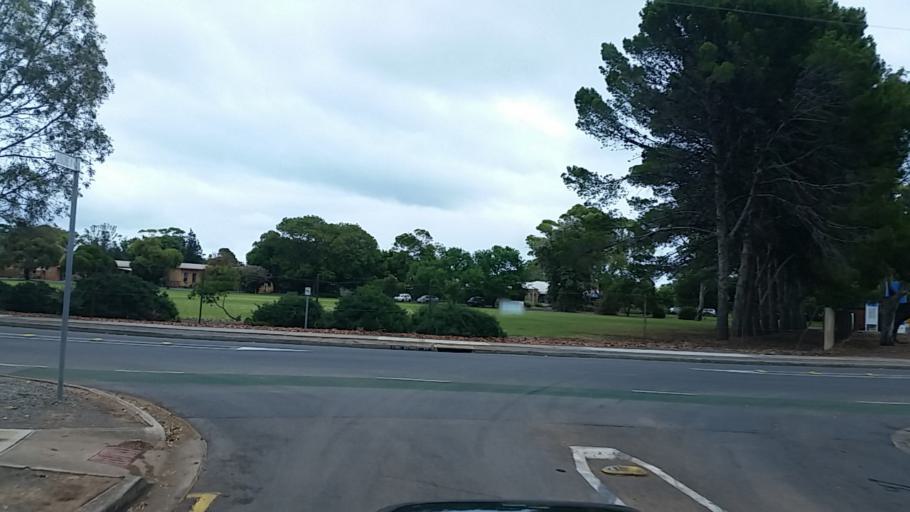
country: AU
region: South Australia
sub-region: Holdfast Bay
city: North Brighton
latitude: -35.0047
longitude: 138.5183
